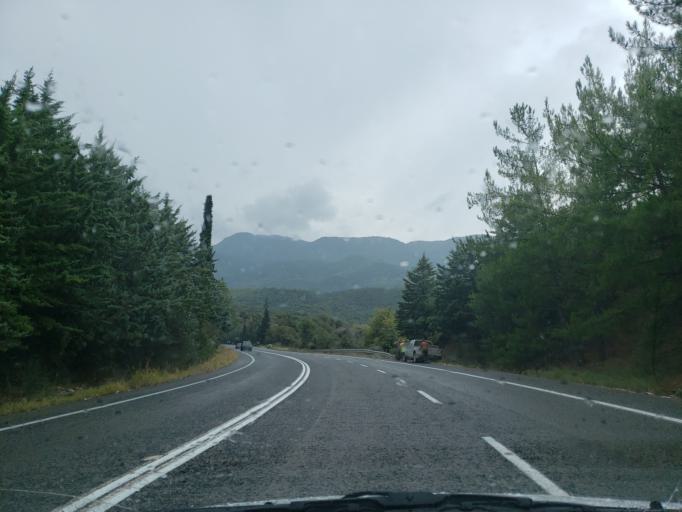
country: GR
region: Central Greece
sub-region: Nomos Fthiotidos
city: Anthili
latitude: 38.7919
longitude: 22.4740
